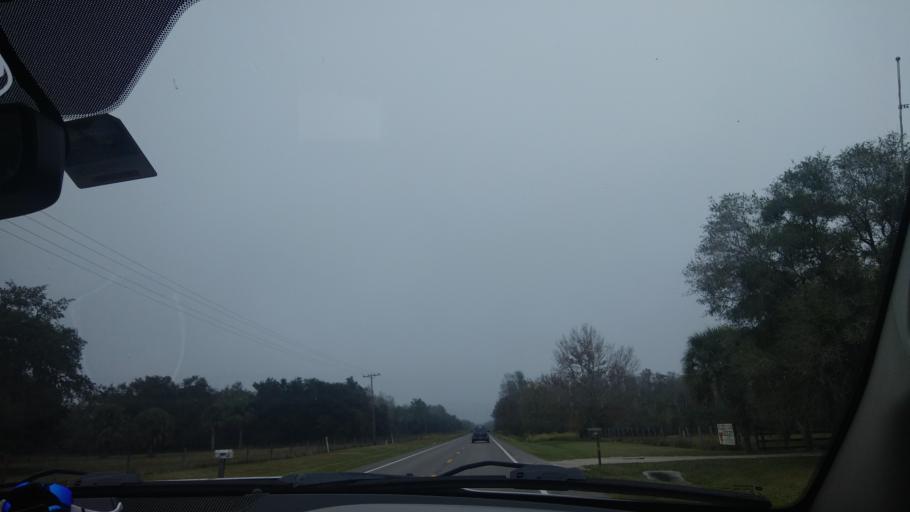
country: US
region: Florida
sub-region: Brevard County
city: June Park
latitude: 27.9234
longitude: -80.9960
